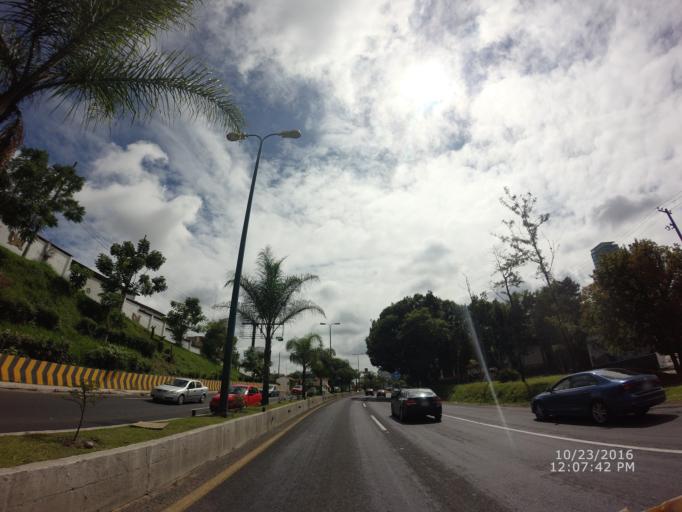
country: MX
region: Veracruz
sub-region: Xalapa
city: Lomas Verdes
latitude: 19.5178
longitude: -96.8817
